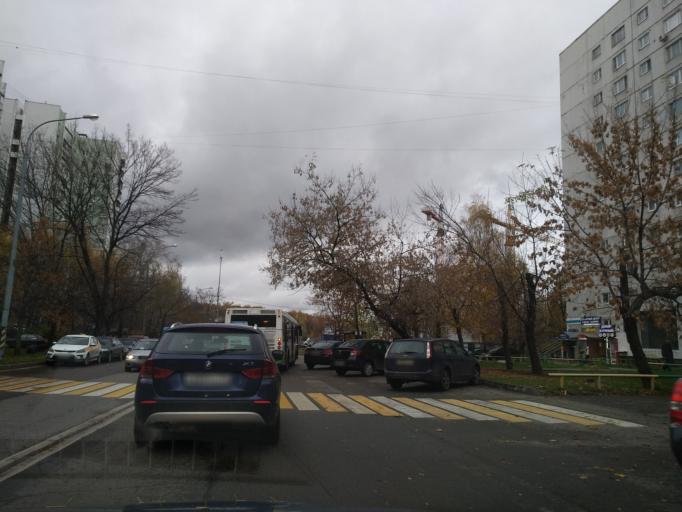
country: RU
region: Moscow
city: Bibirevo
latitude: 55.8961
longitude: 37.6034
